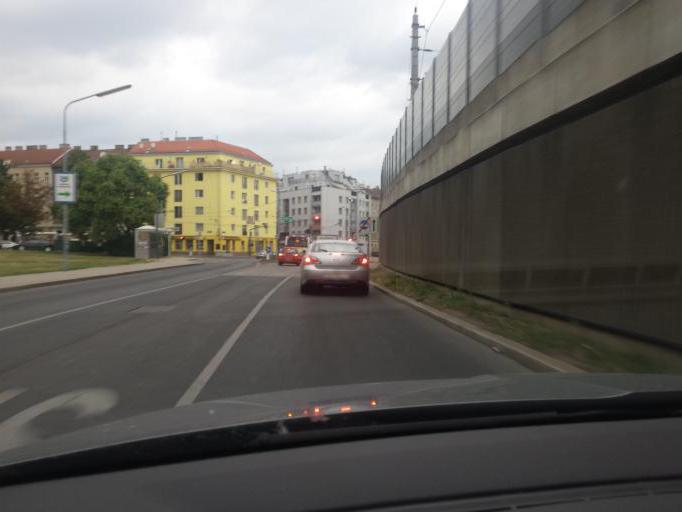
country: AT
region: Vienna
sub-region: Wien Stadt
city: Vienna
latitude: 48.1739
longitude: 16.4070
